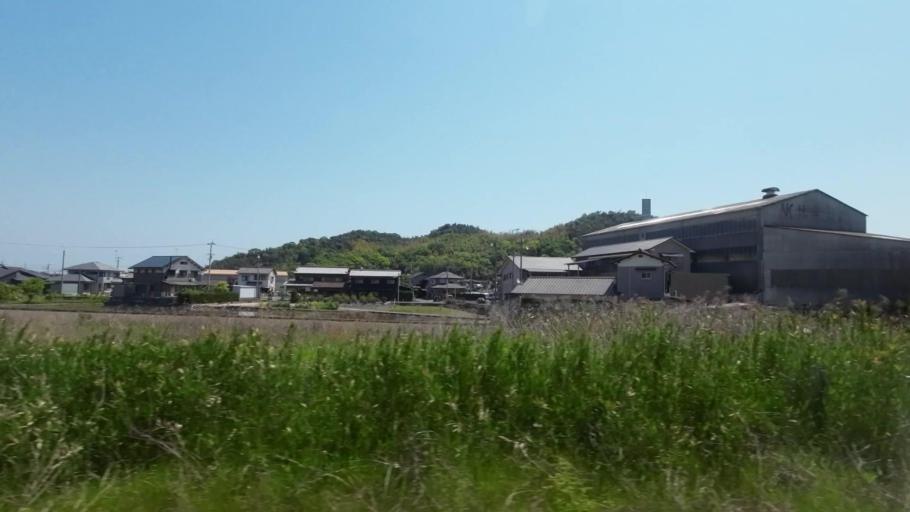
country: JP
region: Ehime
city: Saijo
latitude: 34.0101
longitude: 133.0361
